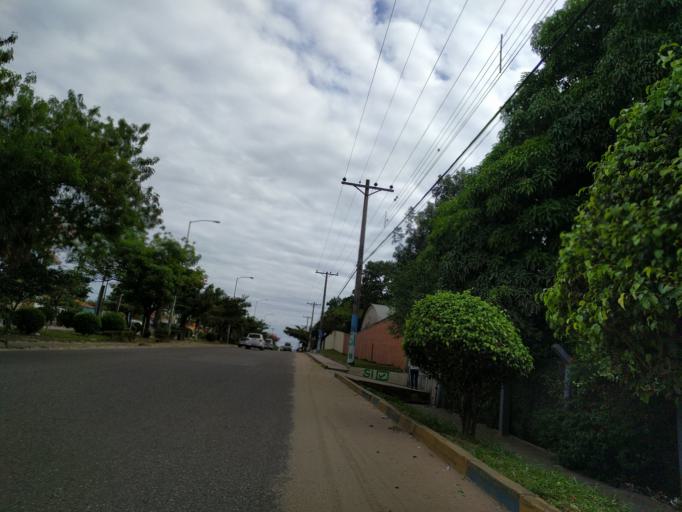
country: BO
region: Santa Cruz
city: Santa Cruz de la Sierra
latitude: -17.8461
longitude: -63.2470
